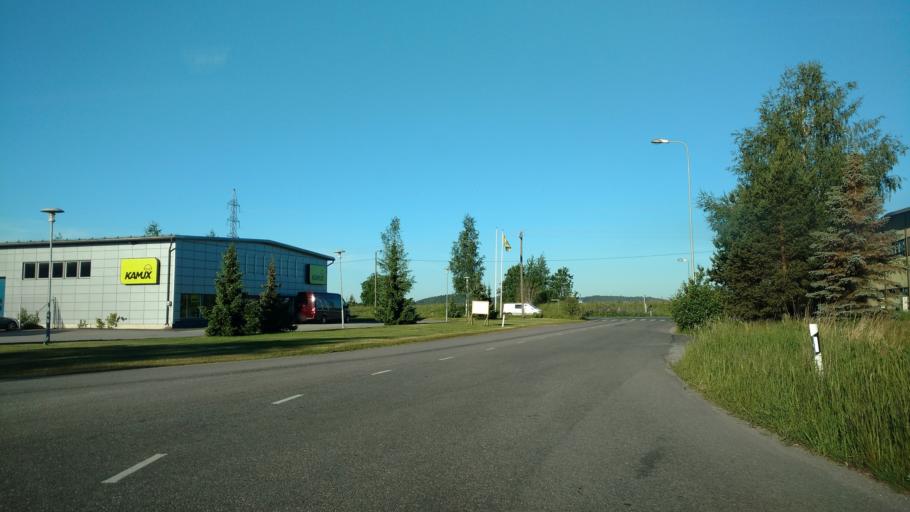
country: FI
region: Varsinais-Suomi
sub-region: Salo
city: Halikko
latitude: 60.3816
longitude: 23.1043
